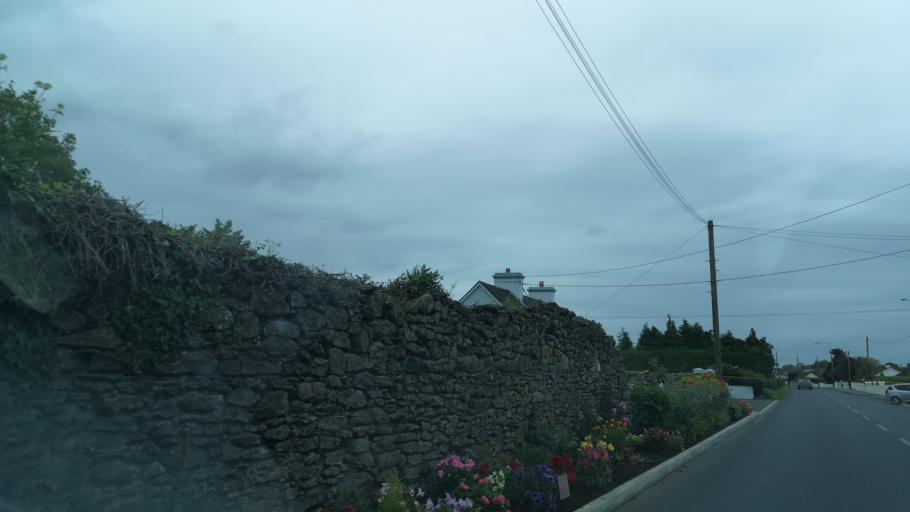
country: IE
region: Leinster
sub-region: Uibh Fhaili
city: Banagher
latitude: 53.1912
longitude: -7.9840
